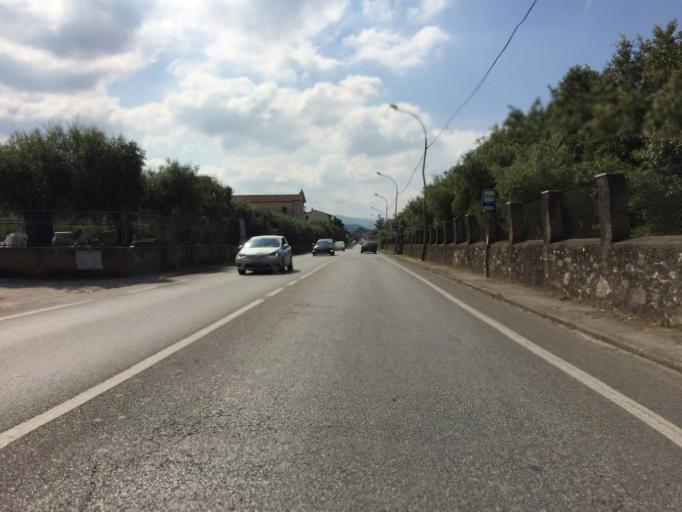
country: IT
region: Tuscany
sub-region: Provincia di Lucca
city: Ripa-Pozzi-Querceta-Ponterosso
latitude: 43.9674
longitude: 10.2128
